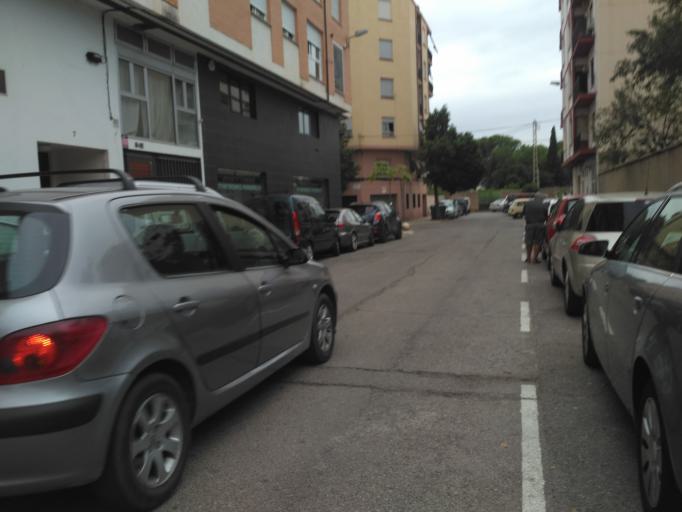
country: ES
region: Valencia
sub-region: Provincia de Castello
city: Castello de la Plana
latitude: 39.9849
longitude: -0.0523
